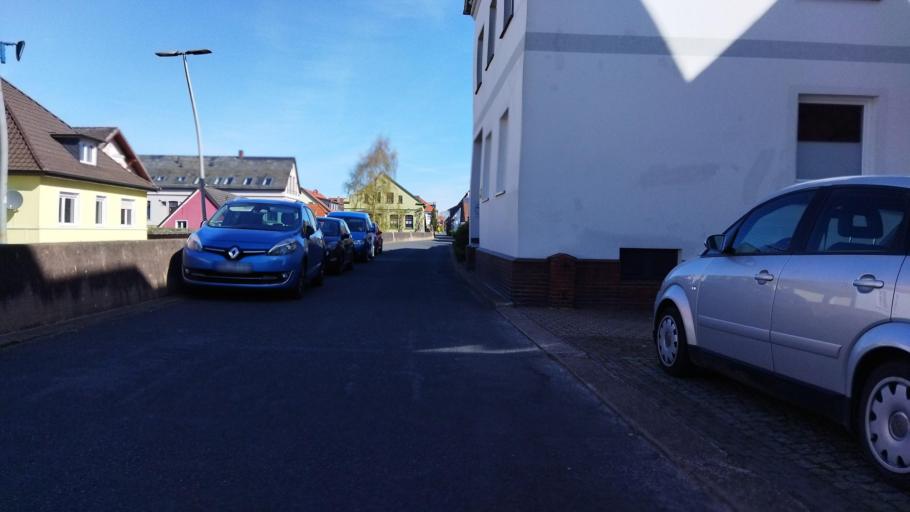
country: DE
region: Lower Saxony
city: Elsfleth
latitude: 53.2380
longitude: 8.4646
